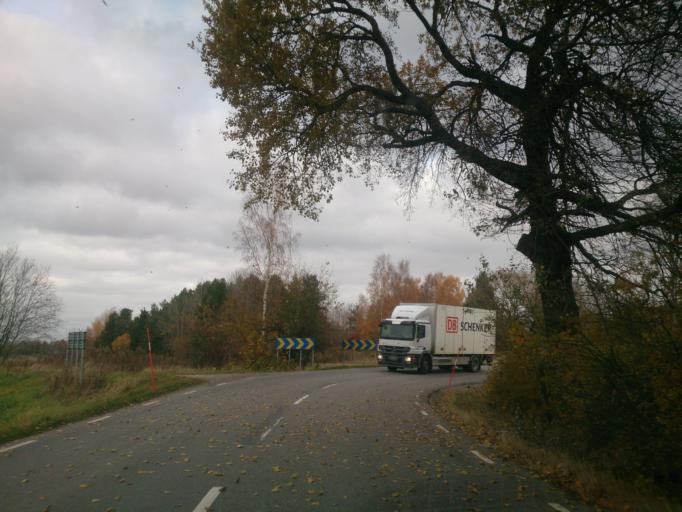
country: SE
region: OEstergoetland
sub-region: Linkopings Kommun
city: Linghem
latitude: 58.4303
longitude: 15.7776
